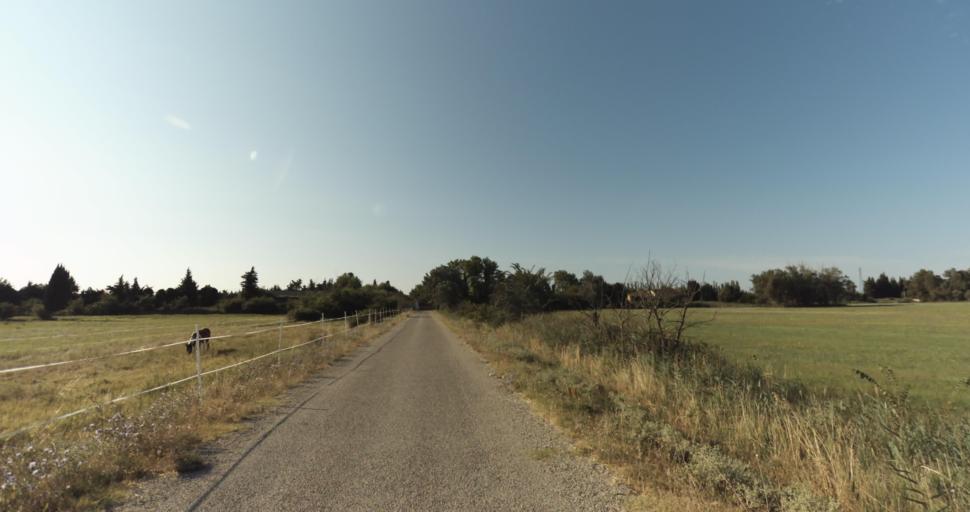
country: FR
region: Provence-Alpes-Cote d'Azur
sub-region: Departement du Vaucluse
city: Sarrians
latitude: 44.0531
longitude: 4.9596
